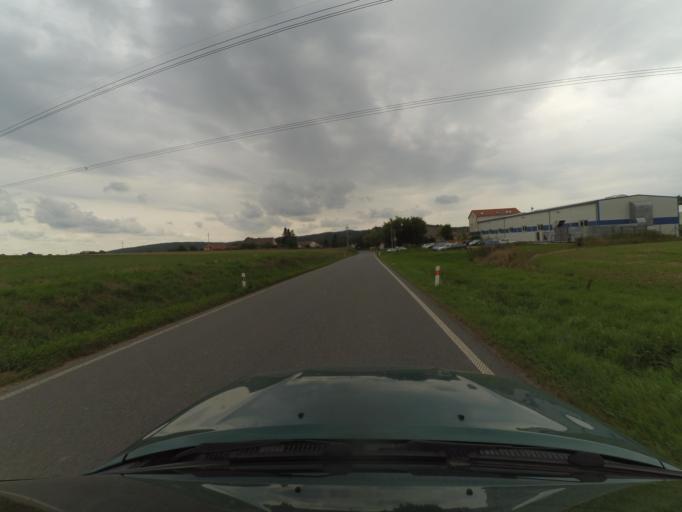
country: CZ
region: Plzensky
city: Chrast
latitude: 49.8440
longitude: 13.5063
